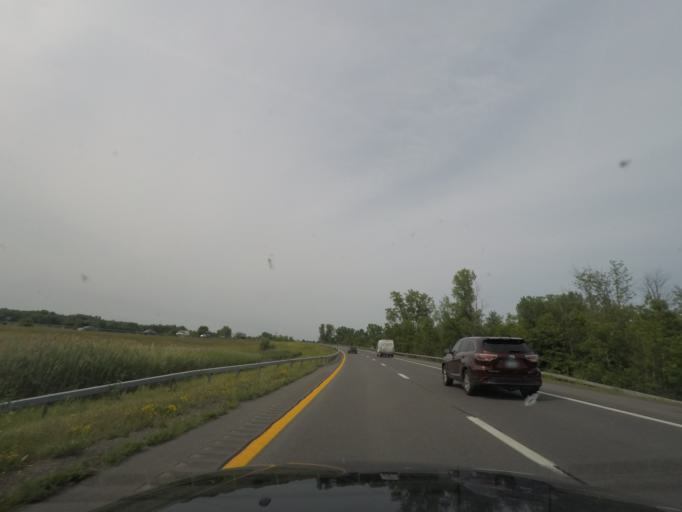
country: US
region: New York
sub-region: Clinton County
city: Plattsburgh West
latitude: 44.6249
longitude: -73.4820
